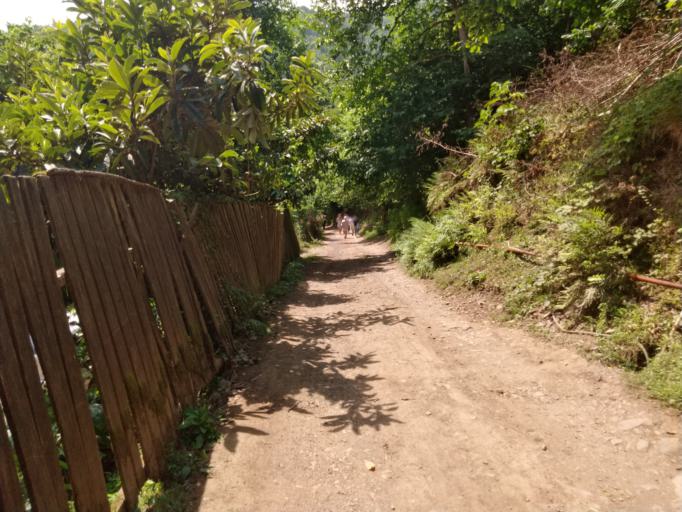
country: TR
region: Artvin
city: Muratli
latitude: 41.5297
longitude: 41.7127
